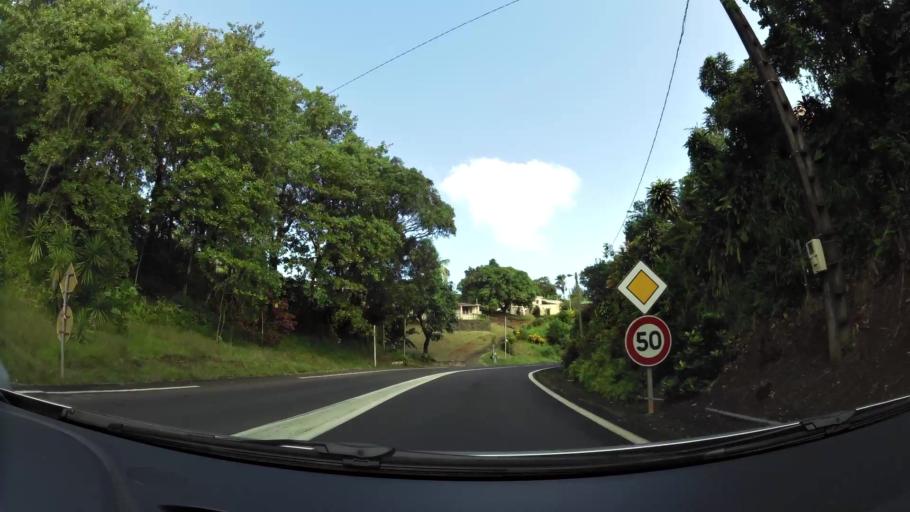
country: MQ
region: Martinique
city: Petite Riviere Salee
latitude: 14.7628
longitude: -60.9819
